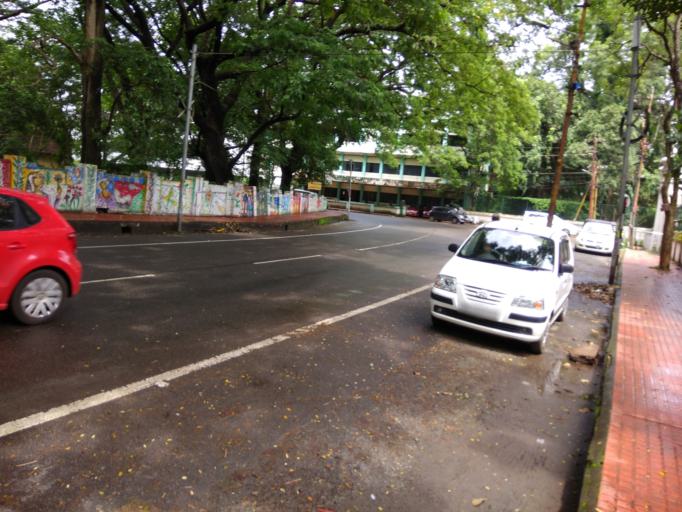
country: IN
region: Kerala
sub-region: Thrissur District
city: Trichur
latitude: 10.5314
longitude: 76.2171
